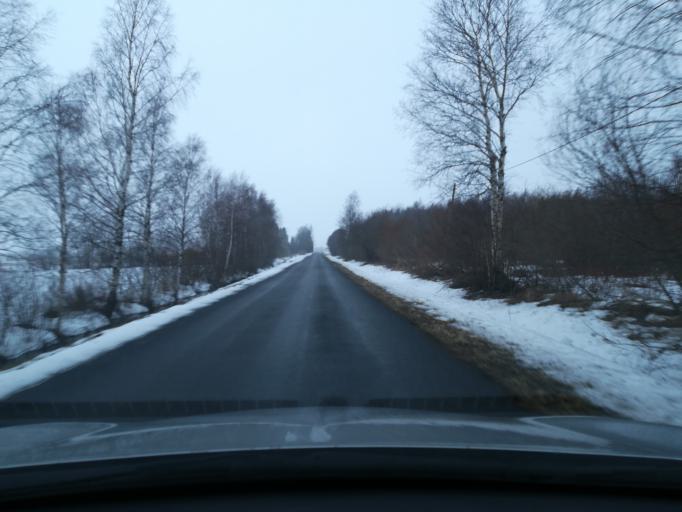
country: EE
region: Harju
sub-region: Raasiku vald
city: Raasiku
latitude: 59.3487
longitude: 25.2122
